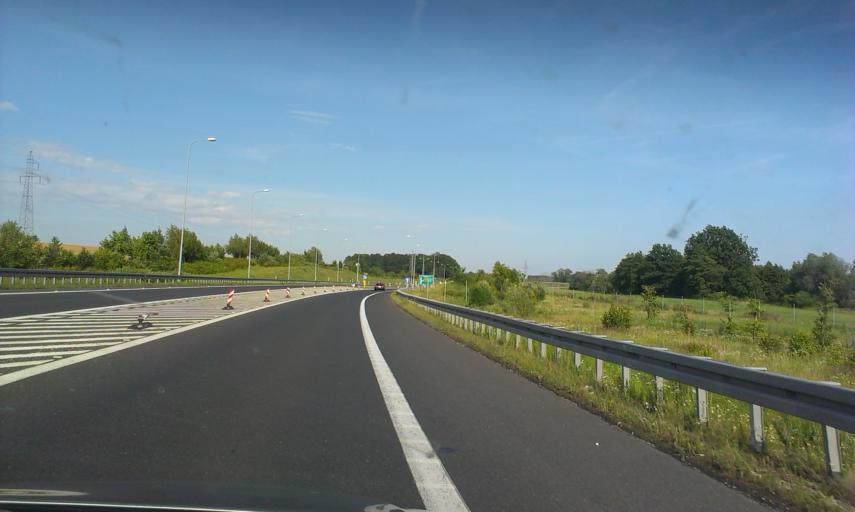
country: PL
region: Greater Poland Voivodeship
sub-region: Powiat pilski
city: Wyrzysk
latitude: 53.1627
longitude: 17.2109
